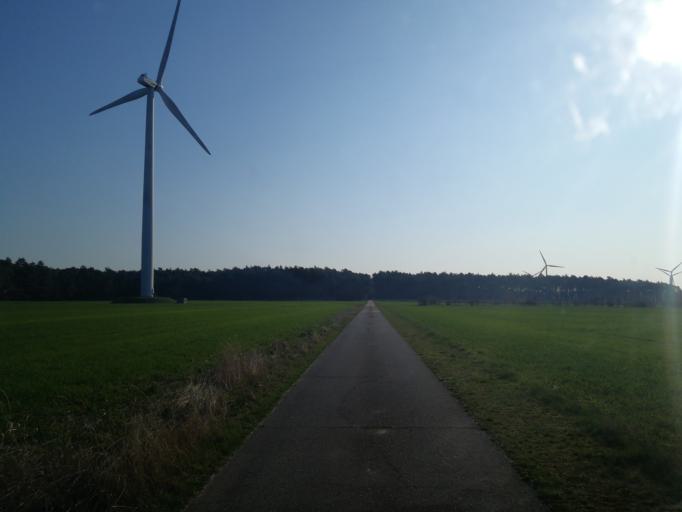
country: DE
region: Brandenburg
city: Drahnsdorf
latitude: 51.8880
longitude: 13.5277
